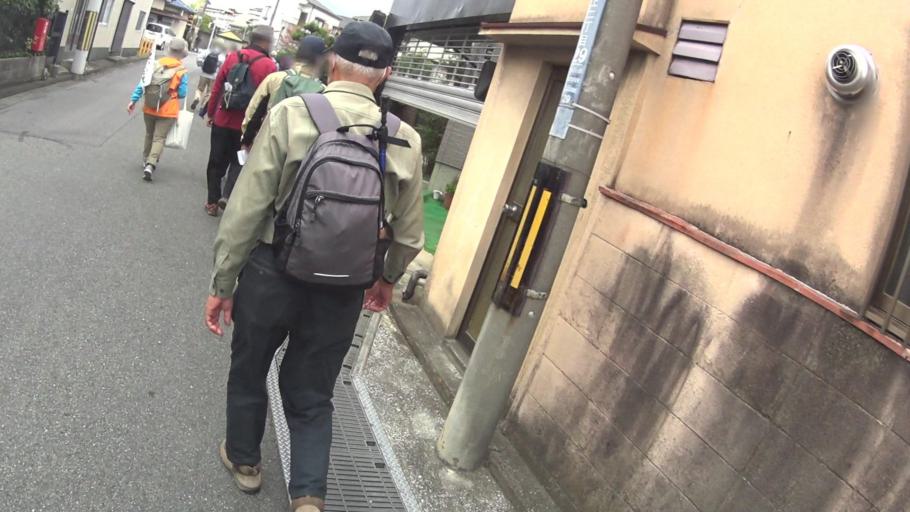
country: JP
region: Osaka
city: Kashihara
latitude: 34.5591
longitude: 135.5930
